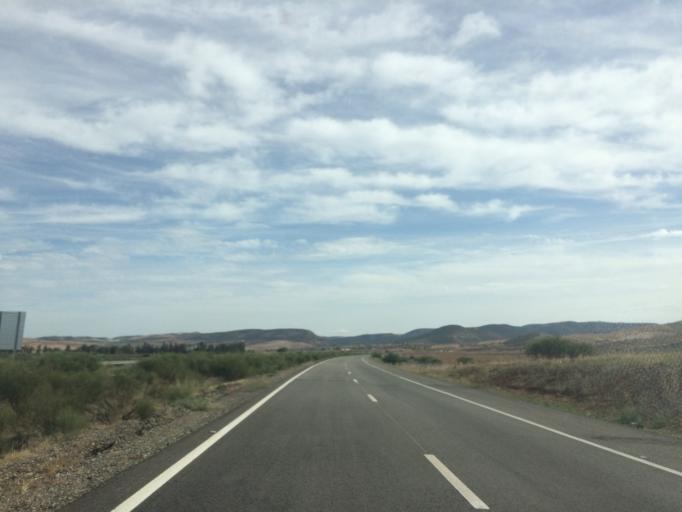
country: MA
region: Rabat-Sale-Zemmour-Zaer
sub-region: Khemisset
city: Khemisset
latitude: 33.7834
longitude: -5.9208
